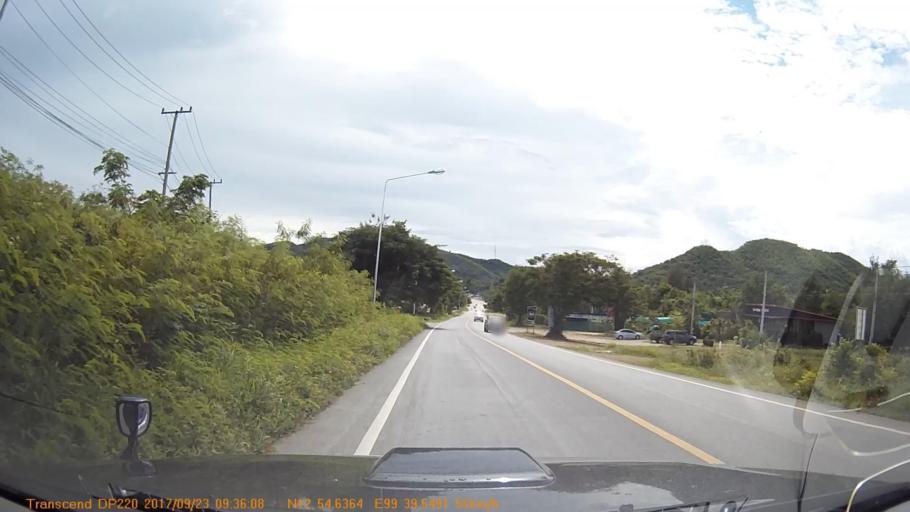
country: TH
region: Phetchaburi
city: Kaeng Krachan
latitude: 12.9105
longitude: 99.6590
